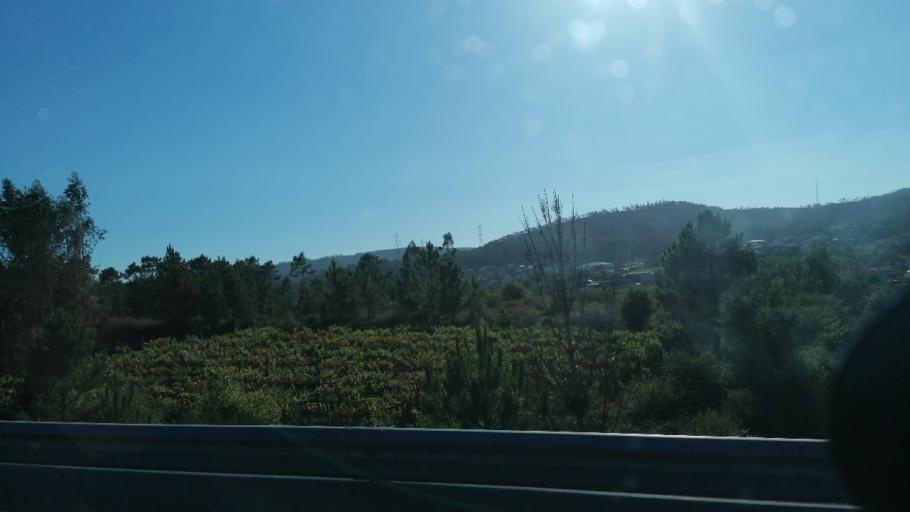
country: PT
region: Porto
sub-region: Valongo
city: Sobrado
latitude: 41.2211
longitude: -8.4497
